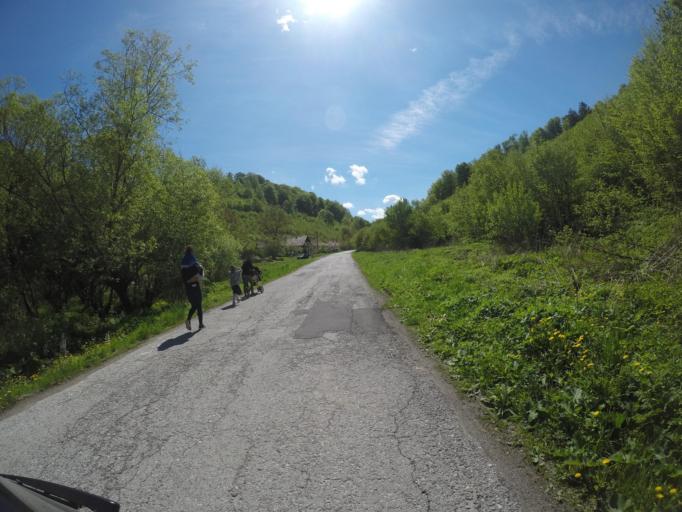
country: SK
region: Banskobystricky
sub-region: Okres Banska Bystrica
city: Banska Bystrica
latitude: 48.7281
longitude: 19.2117
